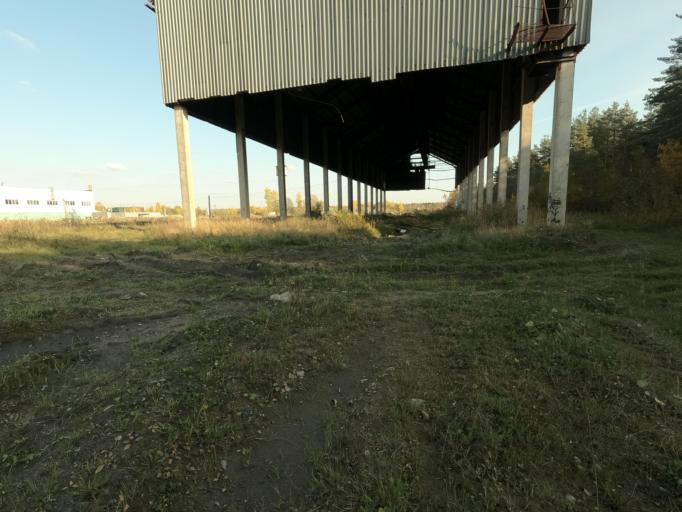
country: RU
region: Leningrad
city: Mga
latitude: 59.7470
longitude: 31.0754
